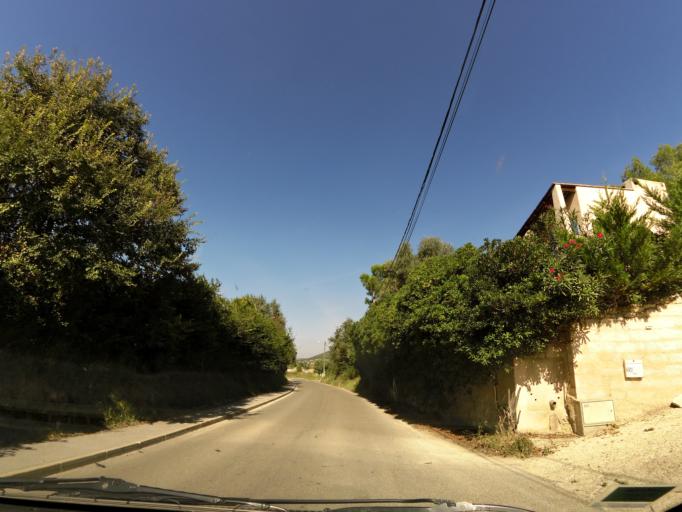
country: FR
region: Languedoc-Roussillon
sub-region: Departement du Gard
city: Nages-et-Solorgues
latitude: 43.7726
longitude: 4.2385
